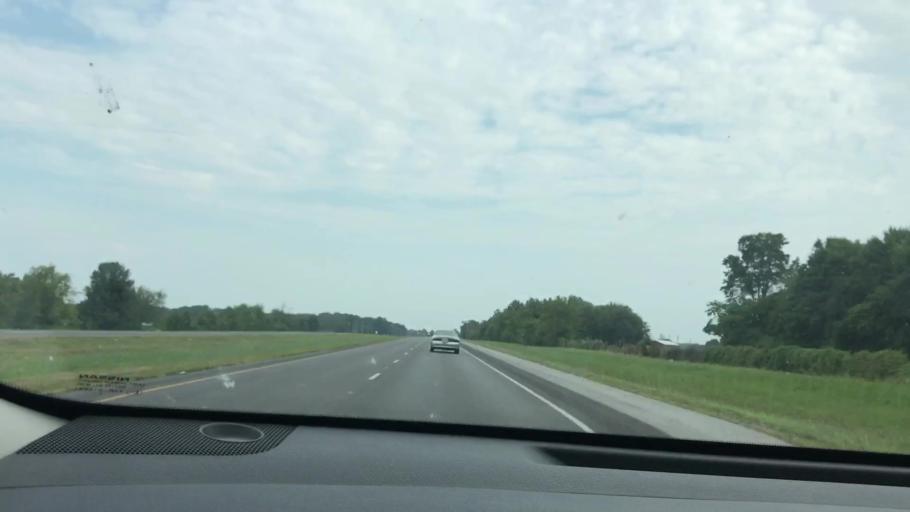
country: US
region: Kentucky
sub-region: Calloway County
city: Murray
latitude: 36.6924
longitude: -88.3030
